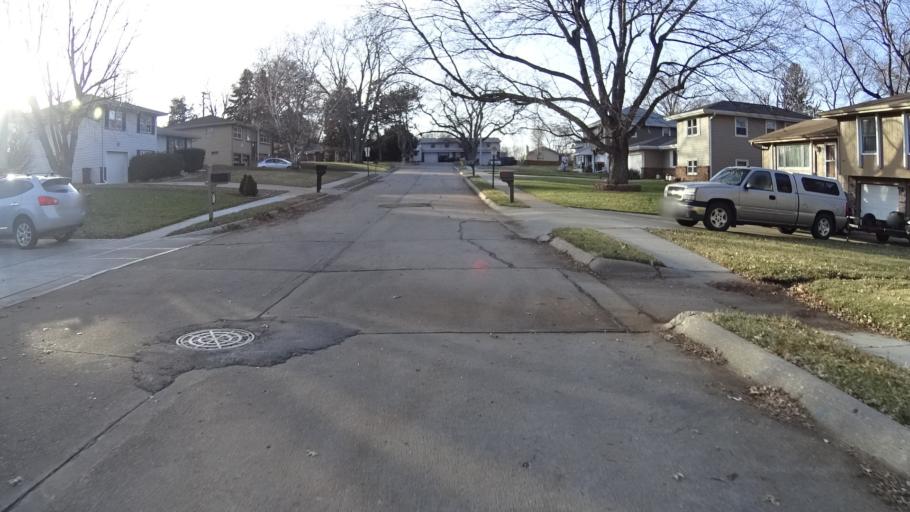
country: US
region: Nebraska
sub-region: Douglas County
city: Ralston
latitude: 41.1913
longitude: -96.0461
